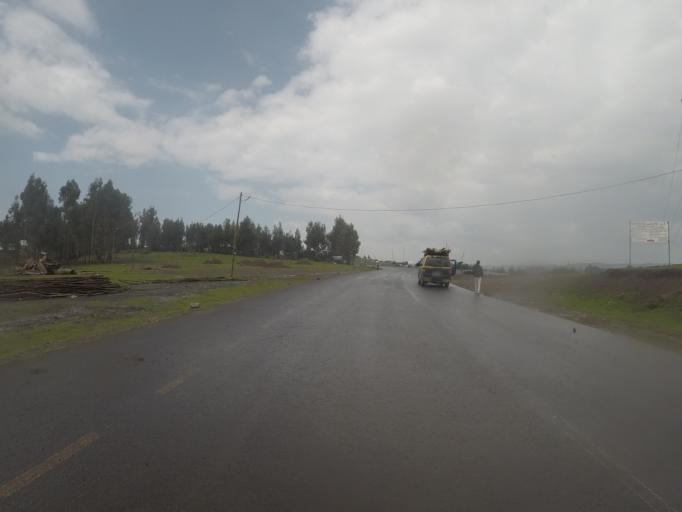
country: ET
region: Amhara
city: Debark'
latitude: 13.1368
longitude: 37.8928
